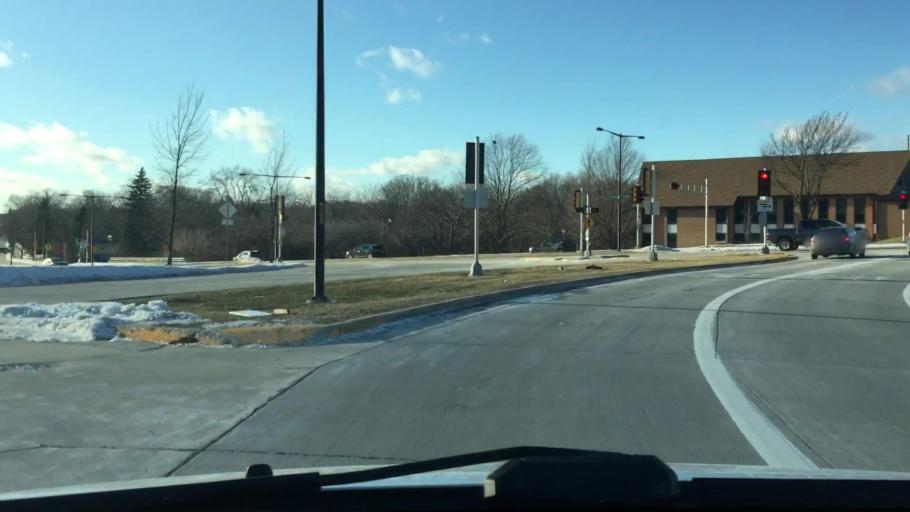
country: US
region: Wisconsin
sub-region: Milwaukee County
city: Greenfield
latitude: 42.9882
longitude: -88.0556
